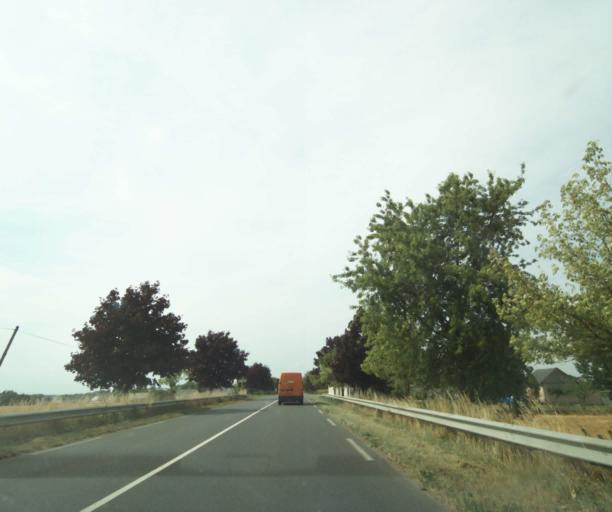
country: FR
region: Centre
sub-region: Departement d'Indre-et-Loire
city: Neuille-Pont-Pierre
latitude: 47.5409
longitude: 0.5559
